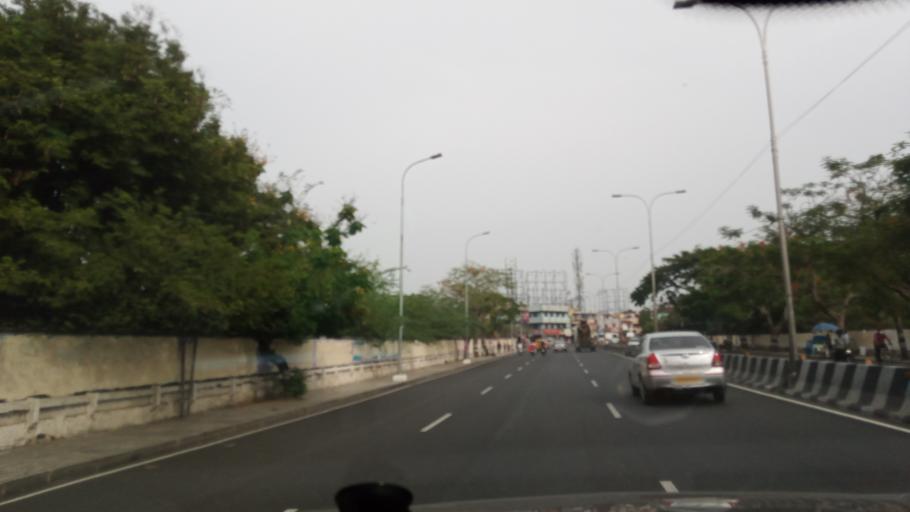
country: IN
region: Tamil Nadu
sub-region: Kancheepuram
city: Saint Thomas Mount
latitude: 13.0120
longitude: 80.1952
